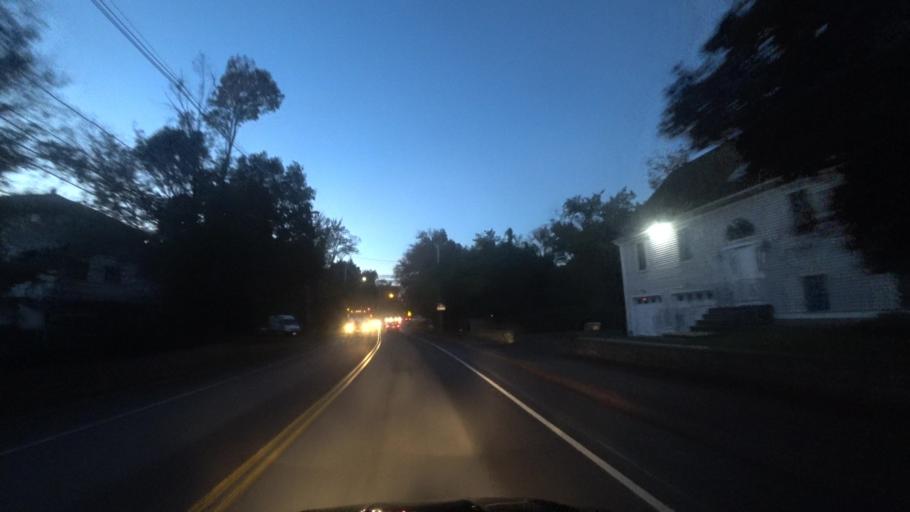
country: US
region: Massachusetts
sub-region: Middlesex County
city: Reading
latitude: 42.5453
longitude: -71.0902
